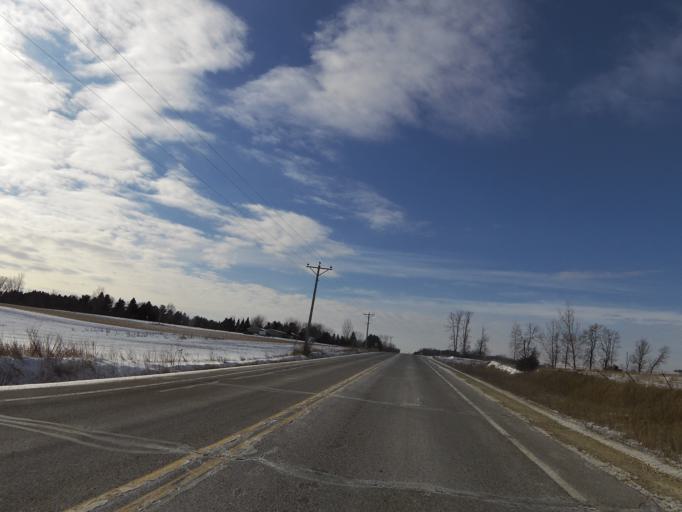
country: US
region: Wisconsin
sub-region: Saint Croix County
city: Roberts
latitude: 44.9927
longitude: -92.5757
